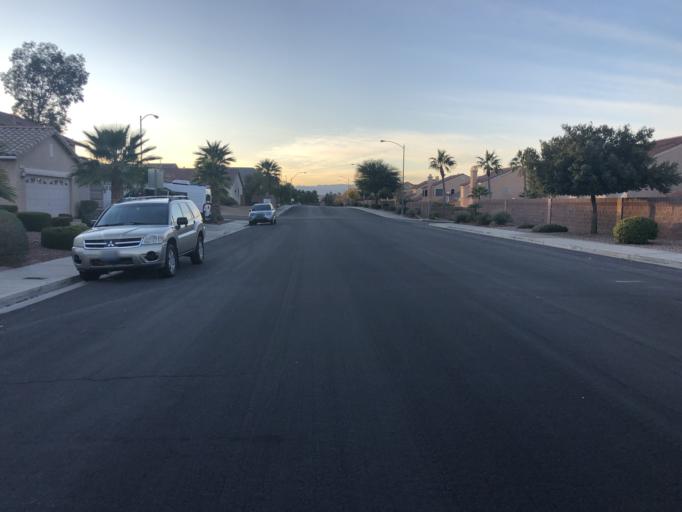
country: US
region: Nevada
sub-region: Clark County
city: Whitney
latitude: 36.0180
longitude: -115.0451
